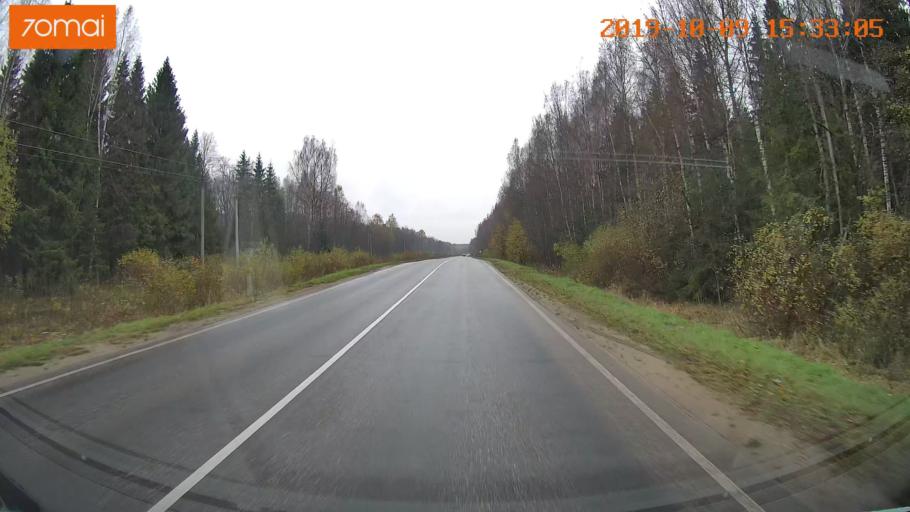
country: RU
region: Kostroma
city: Oktyabr'skiy
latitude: 57.9564
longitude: 41.2671
